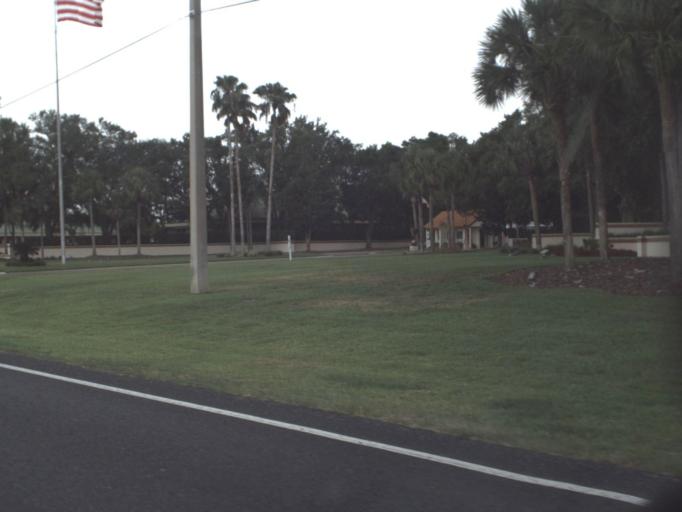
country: US
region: Florida
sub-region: Sumter County
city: The Villages
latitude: 28.9669
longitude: -81.9724
